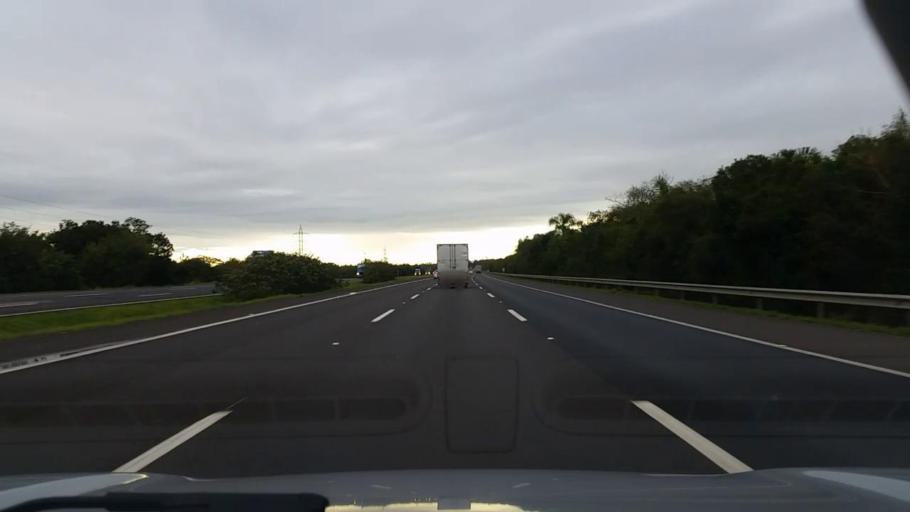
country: BR
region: Rio Grande do Sul
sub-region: Gravatai
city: Gravatai
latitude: -29.9532
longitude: -50.9916
